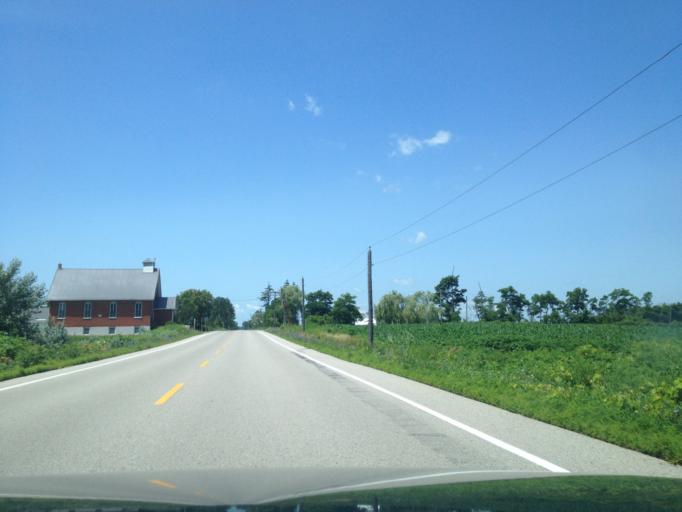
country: CA
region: Ontario
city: Norfolk County
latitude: 42.5786
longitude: -80.5633
